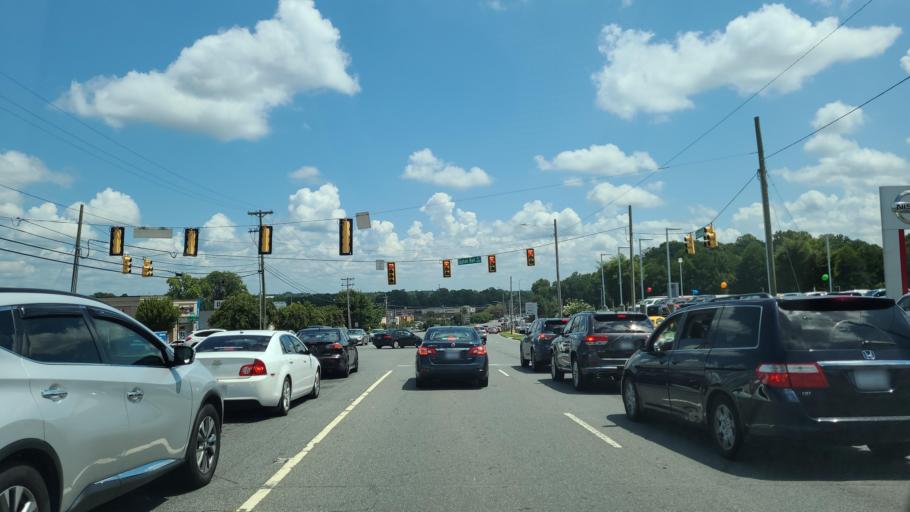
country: US
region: North Carolina
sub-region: Gaston County
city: Ranlo
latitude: 35.2616
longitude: -81.1396
